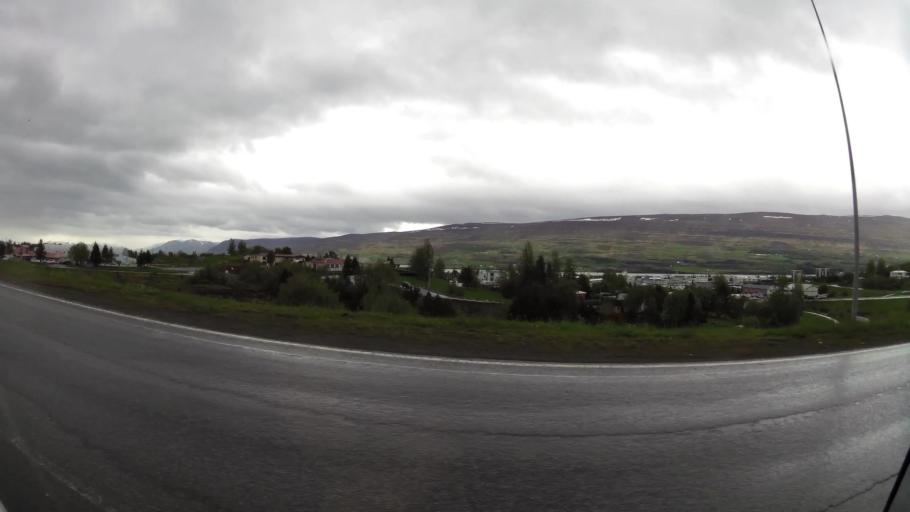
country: IS
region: Northeast
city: Akureyri
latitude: 65.6867
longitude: -18.1165
